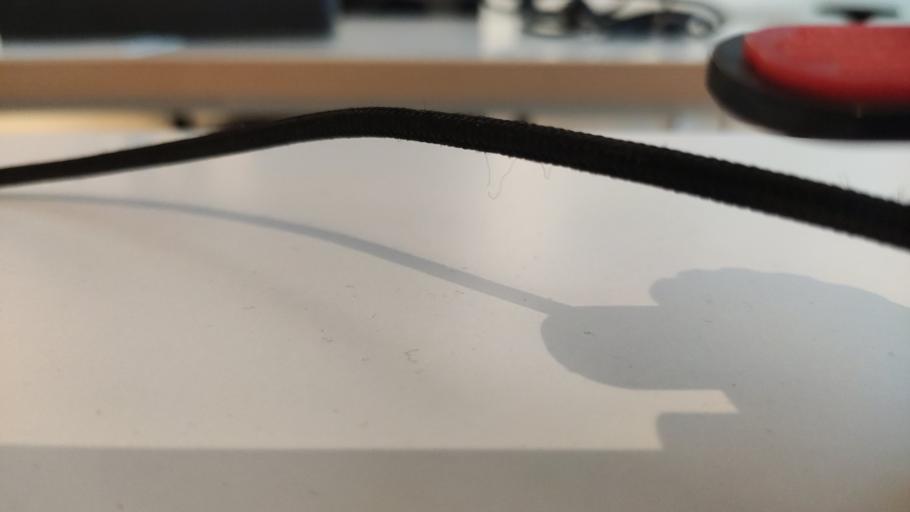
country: RU
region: Moskovskaya
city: Novopetrovskoye
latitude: 55.9133
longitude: 36.4410
